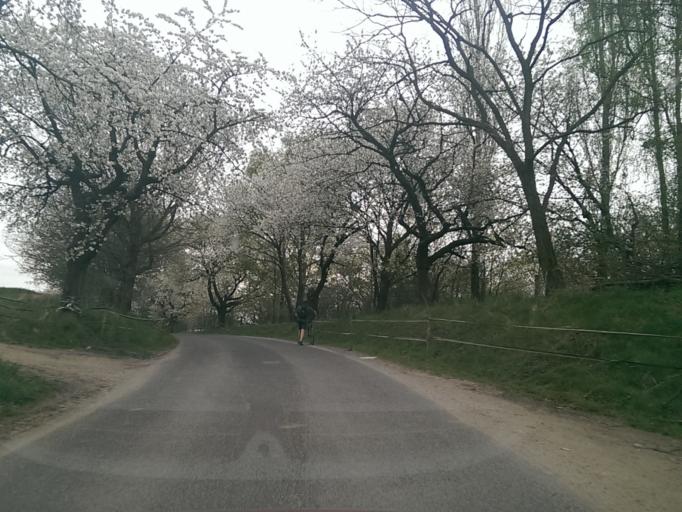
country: CZ
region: Central Bohemia
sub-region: Okres Mlada Boleslav
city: Zd'ar
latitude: 50.5443
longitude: 15.1126
